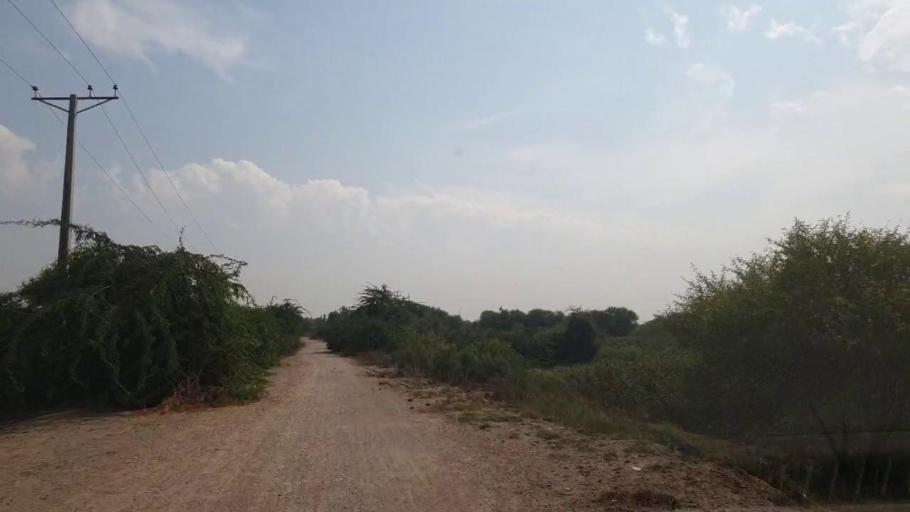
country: PK
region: Sindh
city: Tando Bago
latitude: 24.9318
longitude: 69.0062
